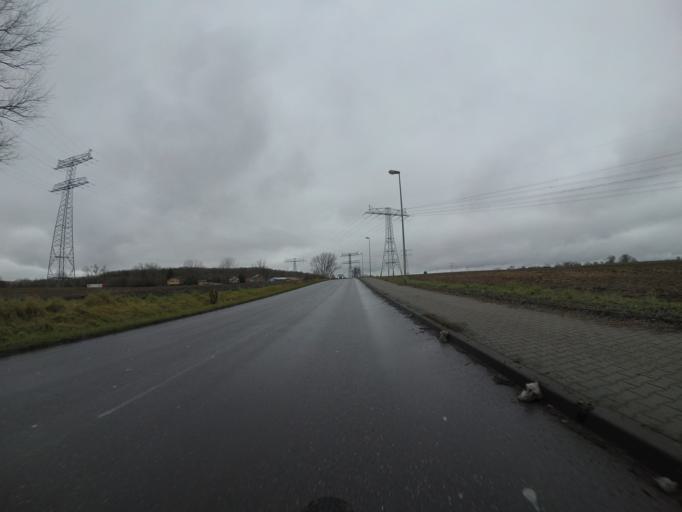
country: DE
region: Berlin
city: Hellersdorf
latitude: 52.5526
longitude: 13.5942
